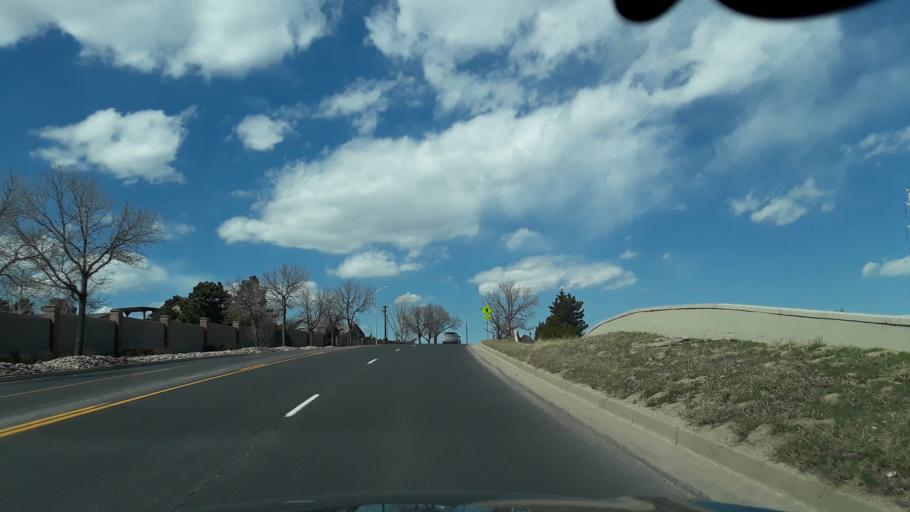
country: US
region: Colorado
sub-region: El Paso County
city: Black Forest
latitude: 38.9389
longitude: -104.7627
